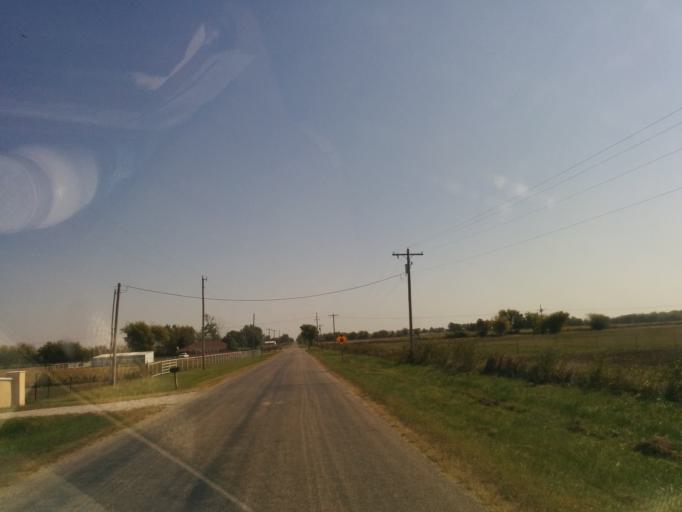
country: US
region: Oklahoma
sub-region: Okmulgee County
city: Beggs
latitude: 35.7990
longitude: -96.0716
